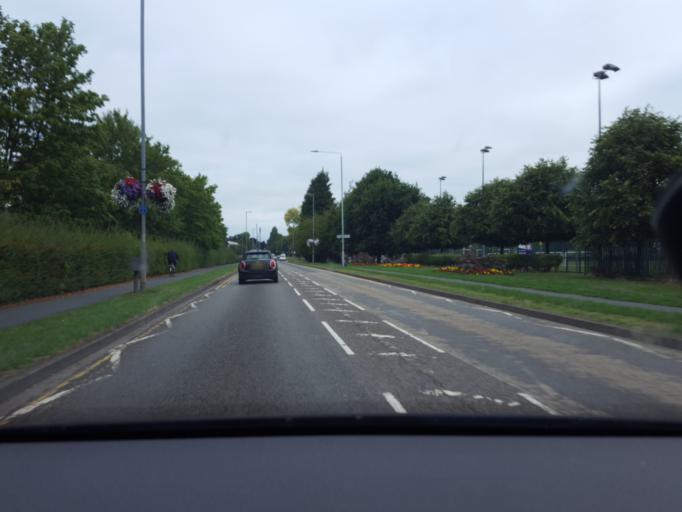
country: GB
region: England
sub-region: Leicestershire
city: Loughborough
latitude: 52.7654
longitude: -1.2196
